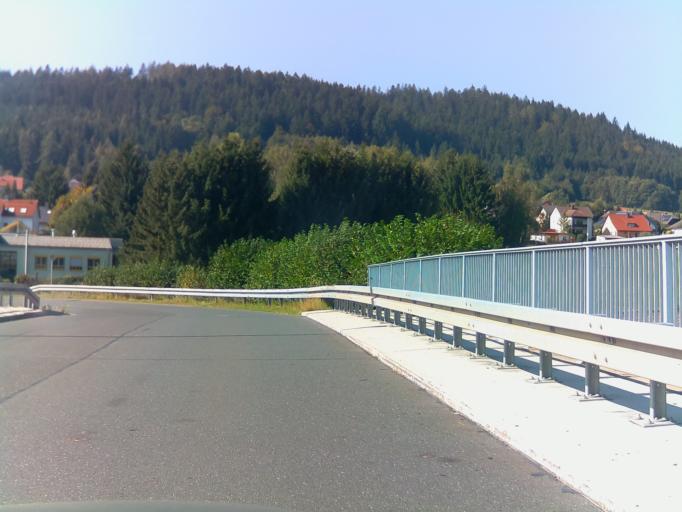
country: DE
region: Bavaria
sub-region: Upper Franconia
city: Pressig
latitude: 50.3523
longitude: 11.3151
